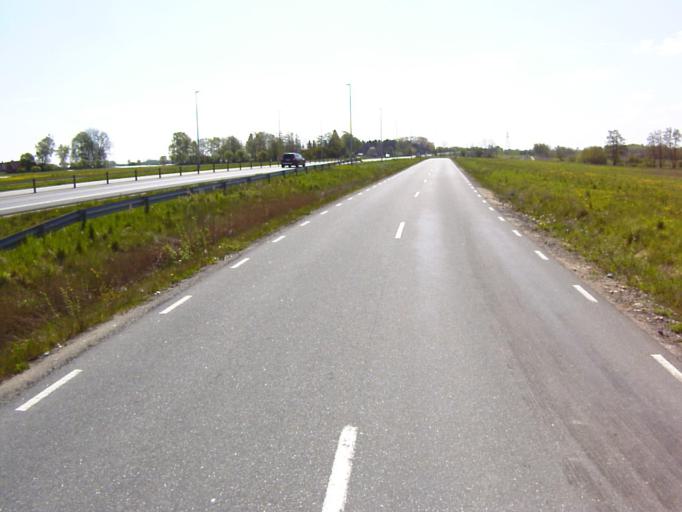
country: SE
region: Skane
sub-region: Kristianstads Kommun
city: Fjalkinge
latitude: 56.0039
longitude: 14.2642
